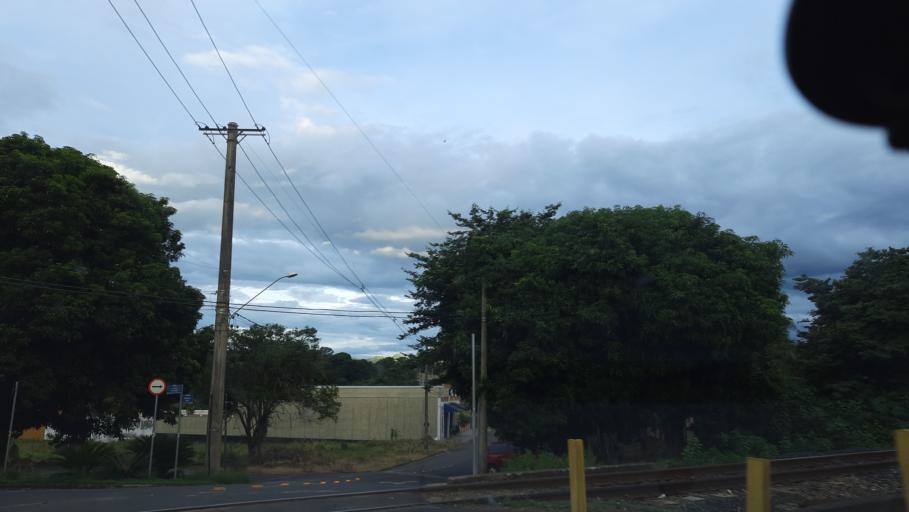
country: BR
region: Sao Paulo
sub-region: Sao Joao Da Boa Vista
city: Sao Joao da Boa Vista
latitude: -21.9640
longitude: -46.7885
